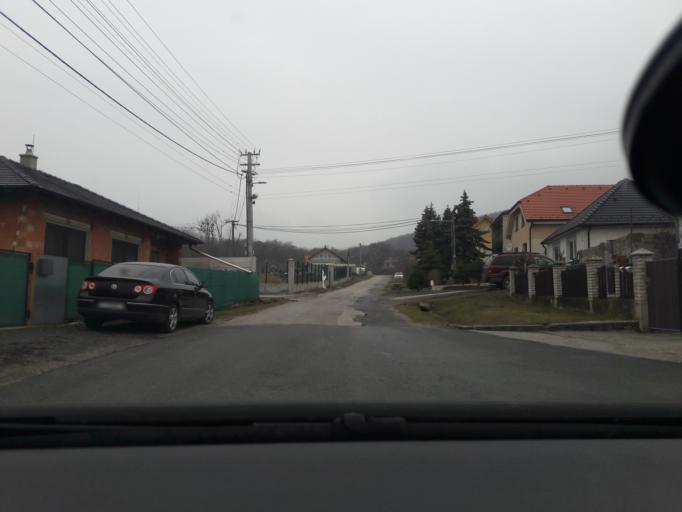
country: SK
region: Trnavsky
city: Smolenice
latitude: 48.4917
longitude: 17.4150
